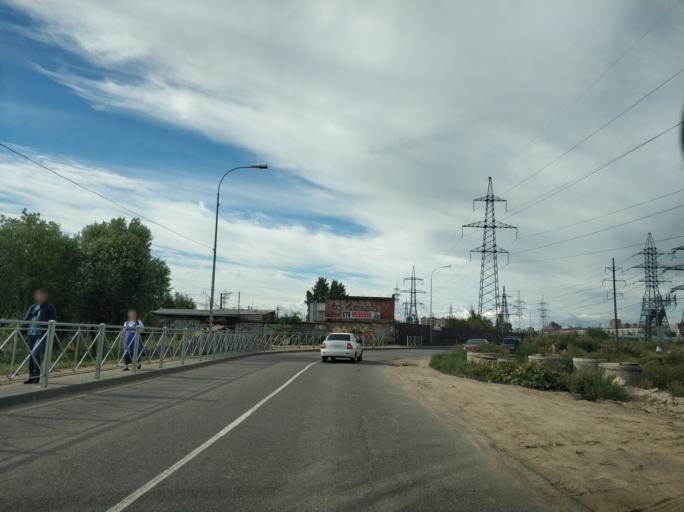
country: RU
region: Leningrad
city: Murino
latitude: 60.0497
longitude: 30.4411
